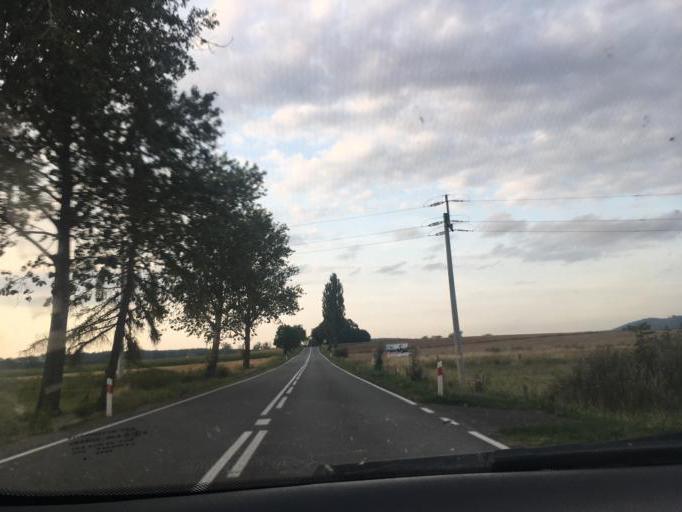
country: PL
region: Lower Silesian Voivodeship
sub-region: Powiat klodzki
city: Bozkow
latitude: 50.5124
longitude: 16.5847
